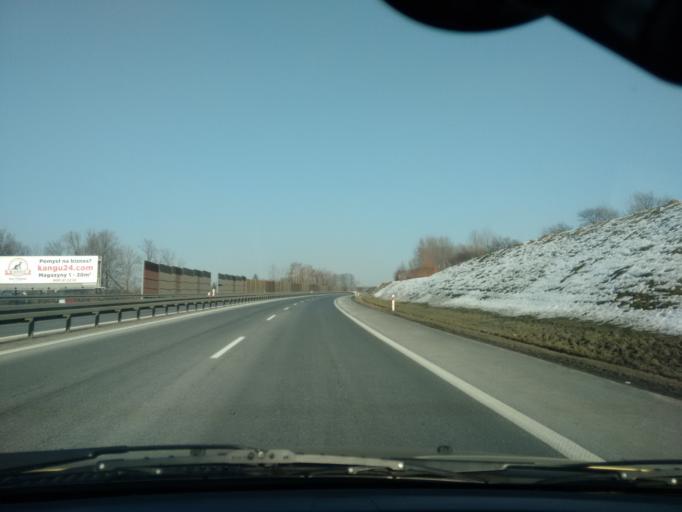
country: PL
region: Silesian Voivodeship
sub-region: Powiat bielski
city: Mazancowice
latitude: 49.8439
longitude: 19.0053
